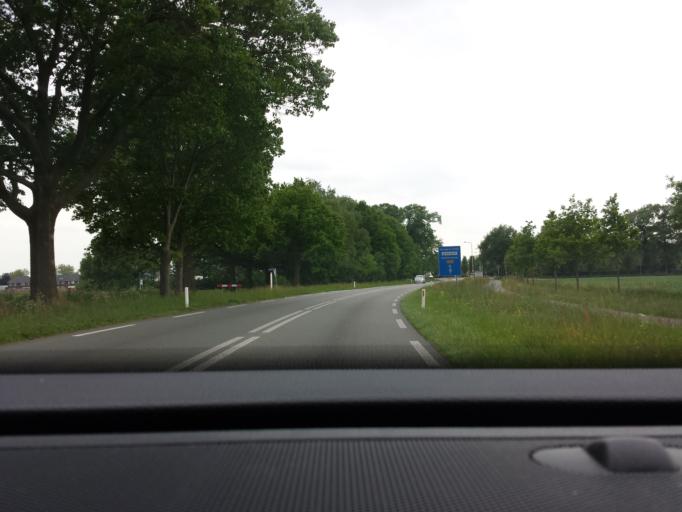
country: NL
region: Gelderland
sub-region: Gemeente Bronckhorst
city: Hengelo
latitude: 52.0605
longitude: 6.3072
